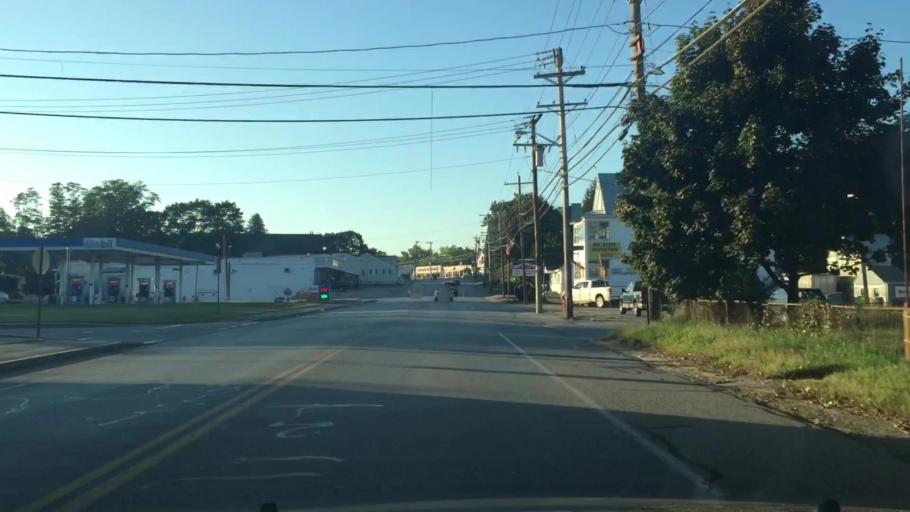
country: US
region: Massachusetts
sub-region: Middlesex County
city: Dracut
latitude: 42.6683
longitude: -71.3253
